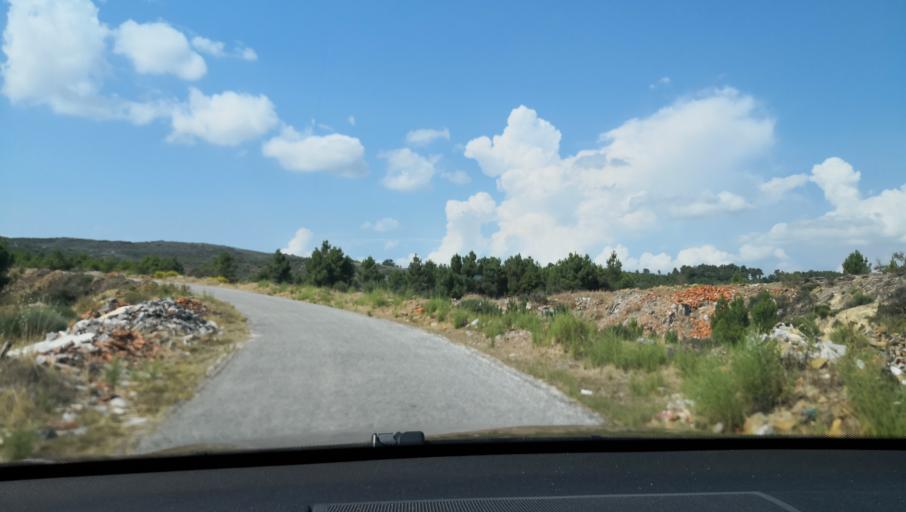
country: PT
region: Vila Real
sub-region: Sabrosa
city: Sabrosa
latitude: 41.3063
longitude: -7.5842
